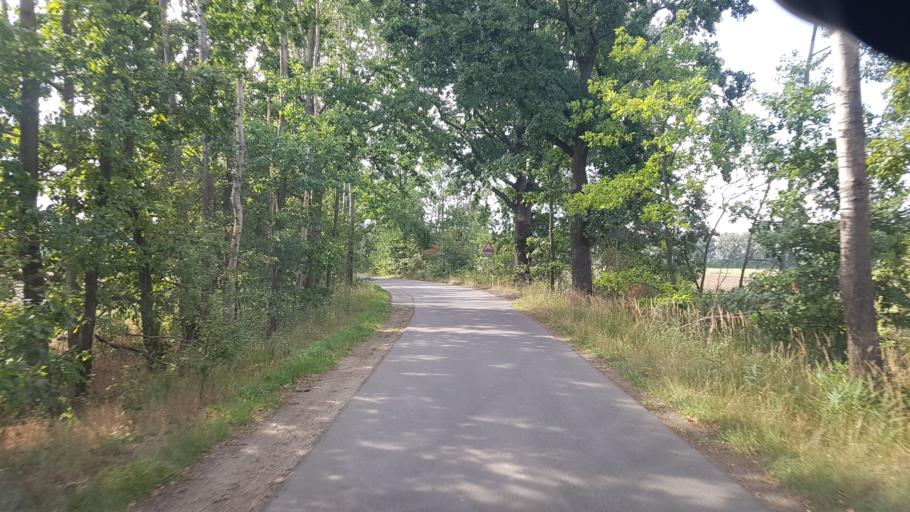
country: DE
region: Brandenburg
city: Plessa
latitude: 51.4395
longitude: 13.6130
